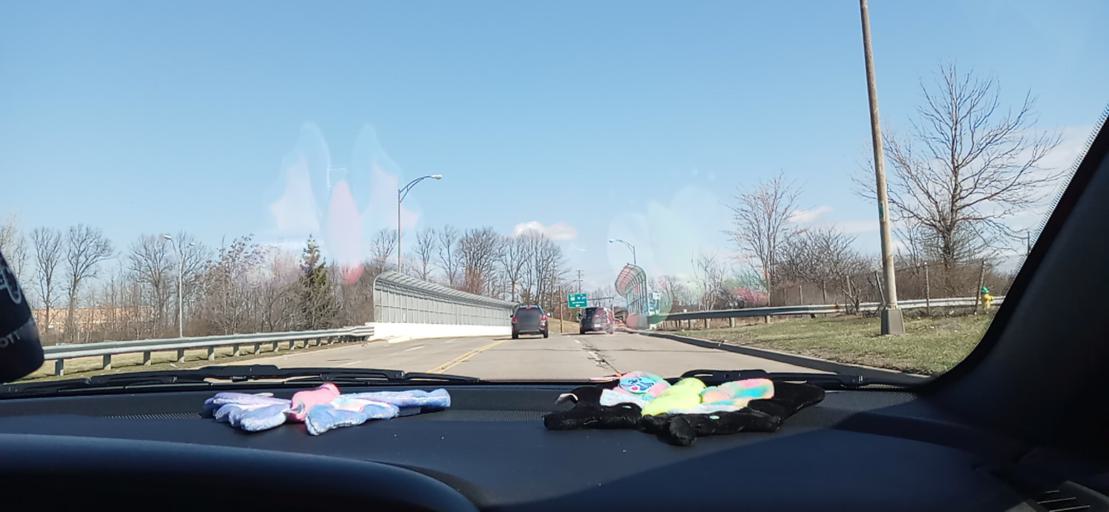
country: US
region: Ohio
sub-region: Summit County
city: Sawyerwood
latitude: 41.0251
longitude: -81.4833
